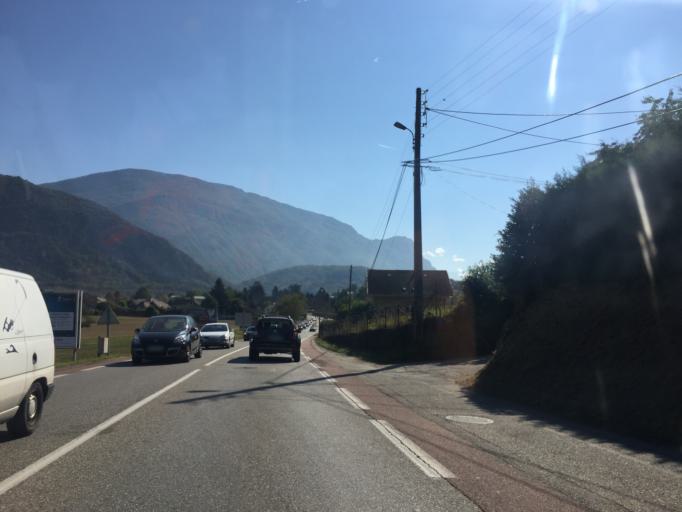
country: FR
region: Rhone-Alpes
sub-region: Departement de la Savoie
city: Challes-les-Eaux
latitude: 45.5452
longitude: 5.9757
